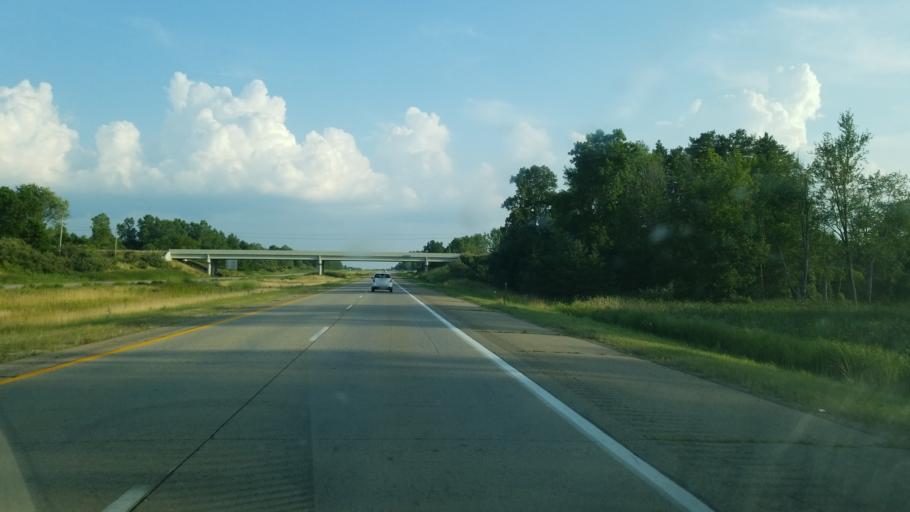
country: US
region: Michigan
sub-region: Clinton County
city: DeWitt
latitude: 42.9093
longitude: -84.5179
